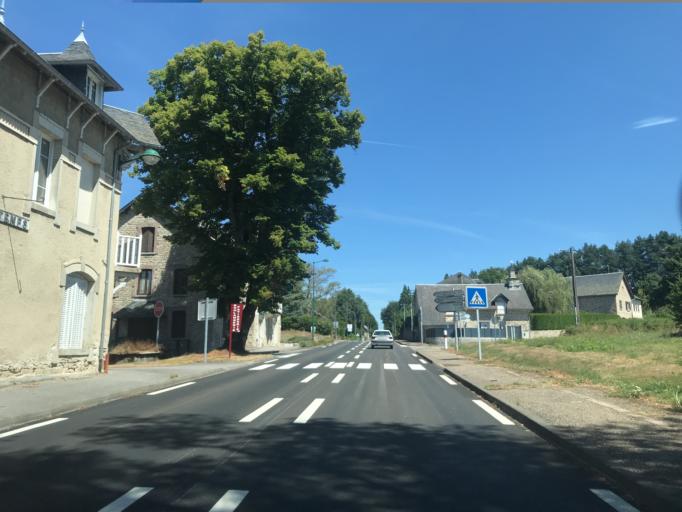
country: FR
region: Limousin
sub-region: Departement de la Correze
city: Egletons
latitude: 45.3771
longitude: 2.0092
